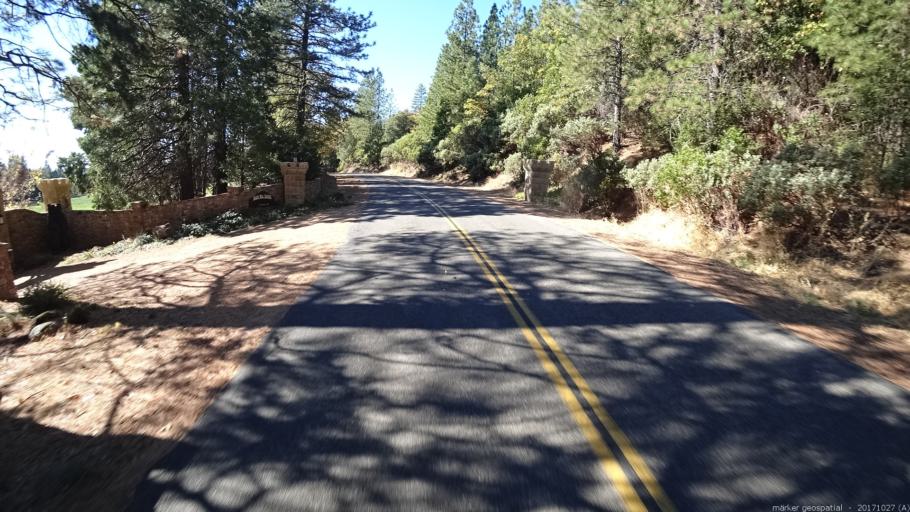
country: US
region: California
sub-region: Shasta County
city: Shingletown
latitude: 40.6904
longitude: -121.9187
